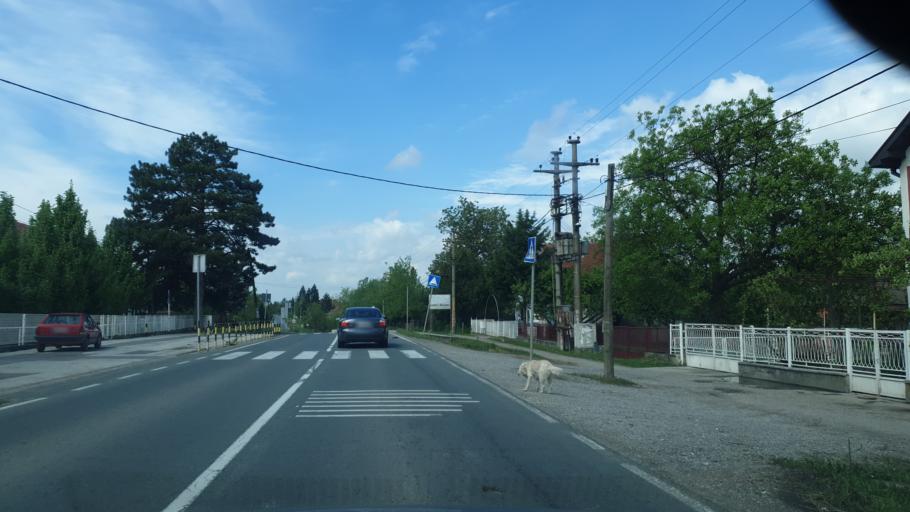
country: RS
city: Stubline
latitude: 44.5740
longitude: 20.1520
